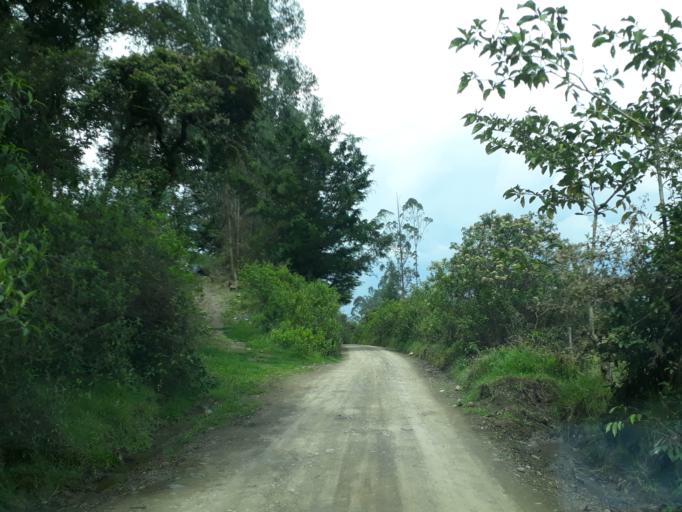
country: CO
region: Cundinamarca
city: Macheta
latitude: 5.0968
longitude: -73.5503
